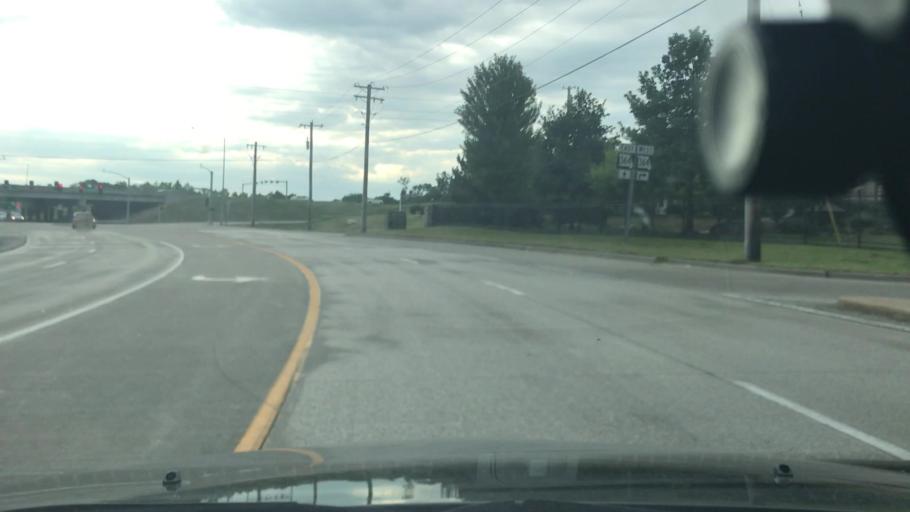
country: US
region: Missouri
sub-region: Saint Charles County
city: Saint Charles
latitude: 38.7451
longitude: -90.5277
